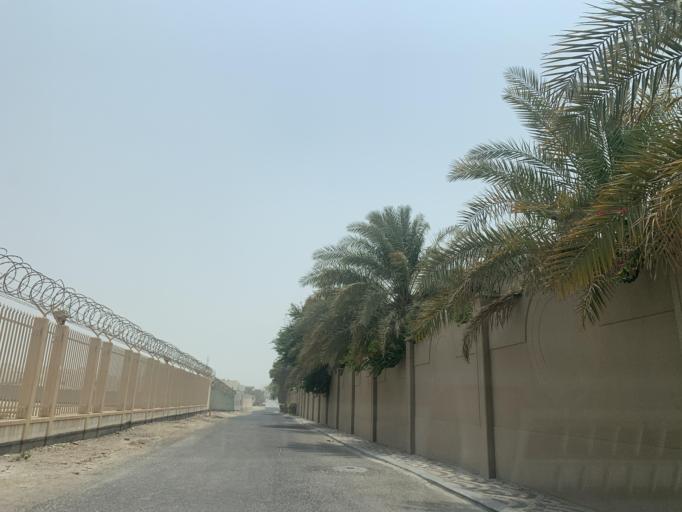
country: BH
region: Central Governorate
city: Madinat Hamad
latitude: 26.1667
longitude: 50.4792
